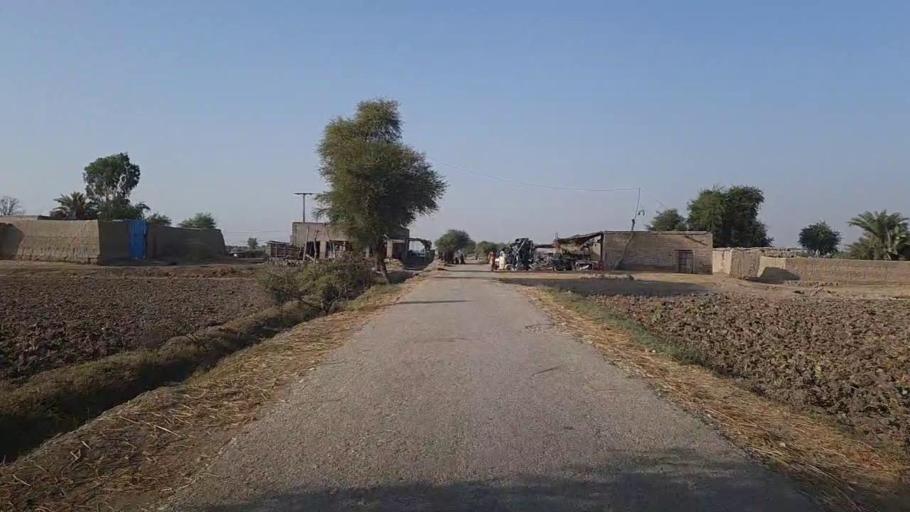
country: PK
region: Sindh
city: Kashmor
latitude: 28.4130
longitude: 69.4114
